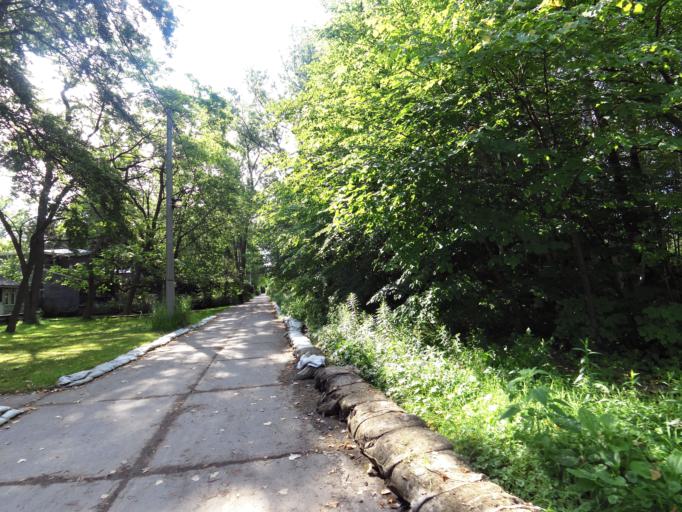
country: CA
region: Ontario
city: Toronto
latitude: 43.6271
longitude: -79.3617
